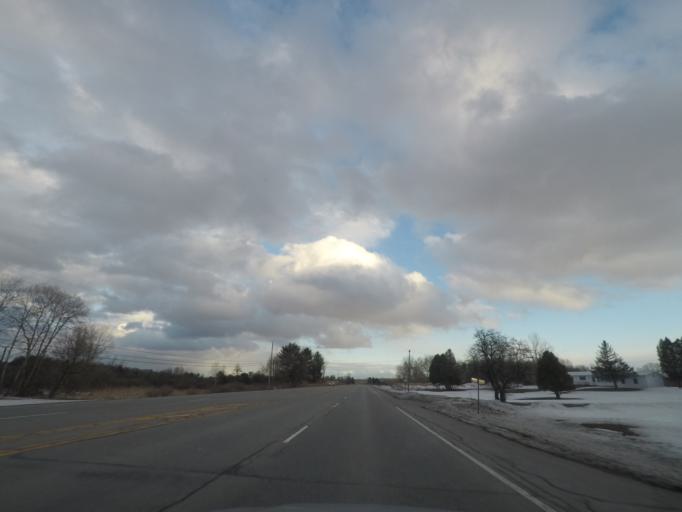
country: US
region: New York
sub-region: Herkimer County
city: Dolgeville
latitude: 43.0201
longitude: -74.7799
